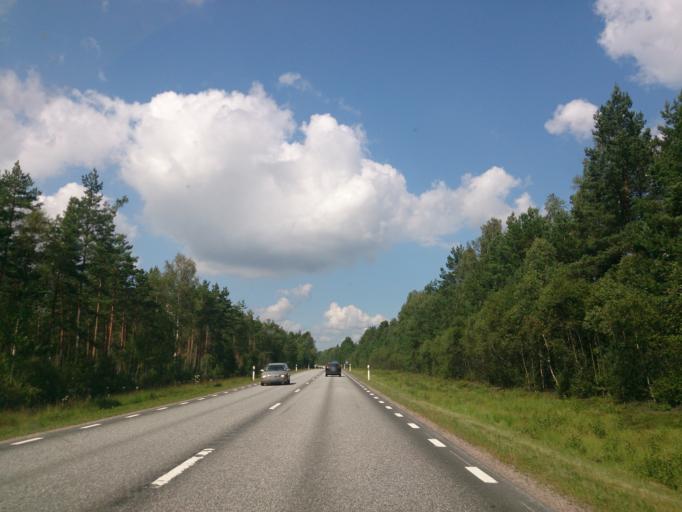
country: SE
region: Joenkoeping
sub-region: Varnamo Kommun
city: Forsheda
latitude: 57.1669
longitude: 13.7855
